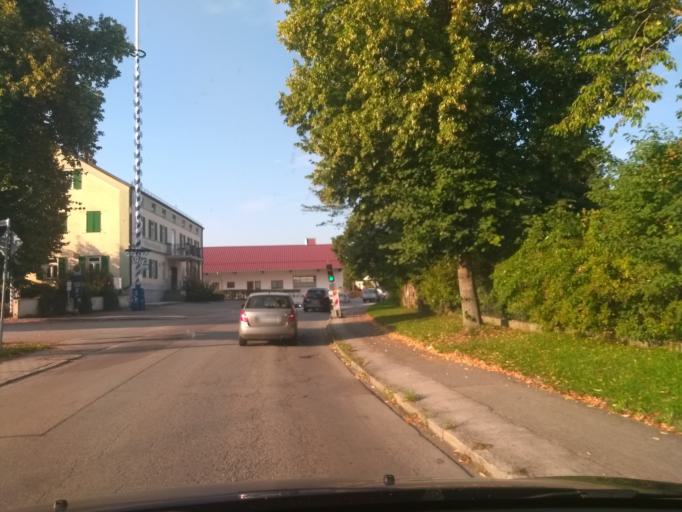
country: DE
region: Bavaria
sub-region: Upper Bavaria
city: Schwabhausen
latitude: 48.3202
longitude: 11.3864
